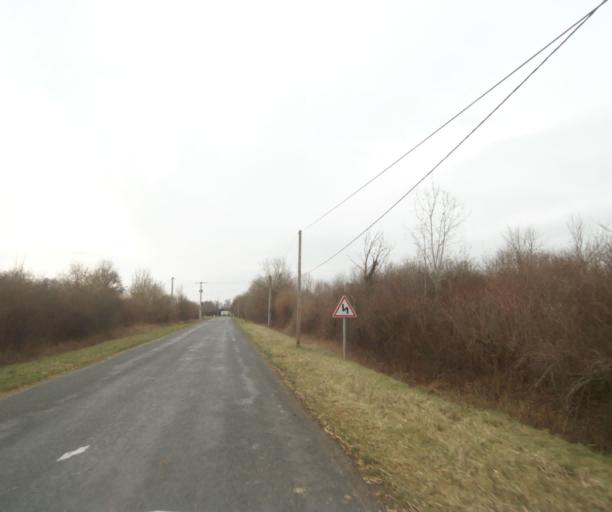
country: FR
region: Champagne-Ardenne
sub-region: Departement de la Haute-Marne
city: Villiers-en-Lieu
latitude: 48.6501
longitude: 4.8744
